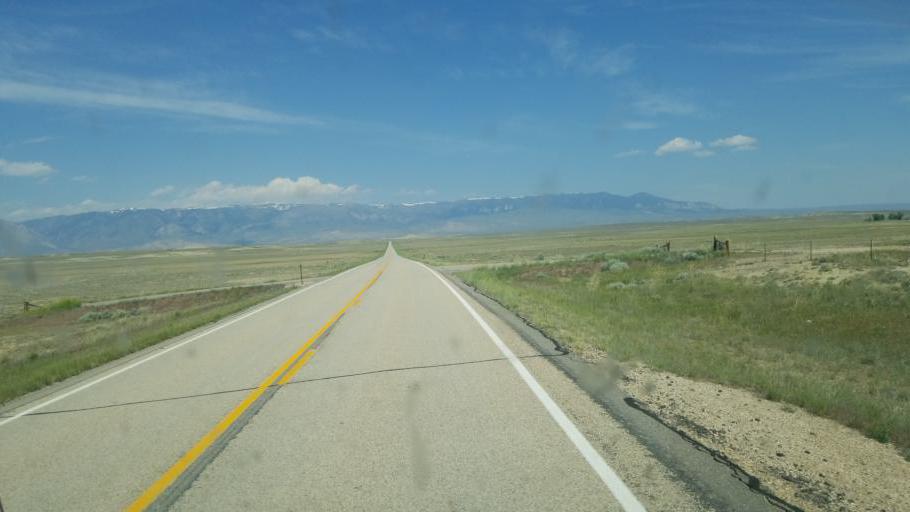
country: US
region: Wyoming
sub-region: Park County
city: Powell
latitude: 44.8574
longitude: -109.0202
